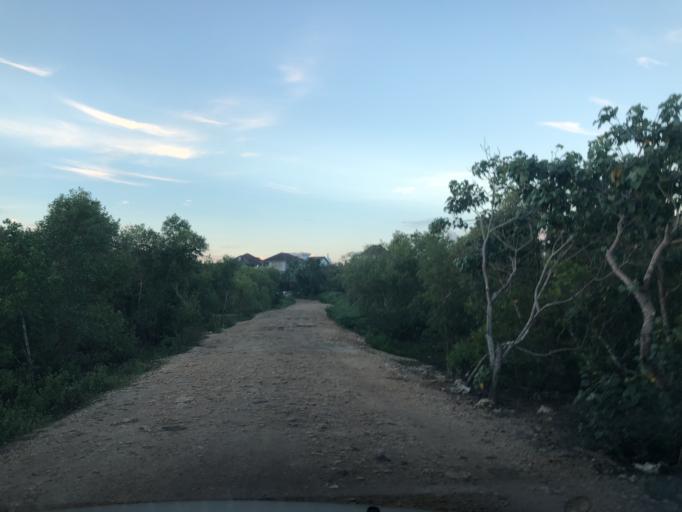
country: TZ
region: Zanzibar Urban/West
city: Zanzibar
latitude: -6.2233
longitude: 39.2091
